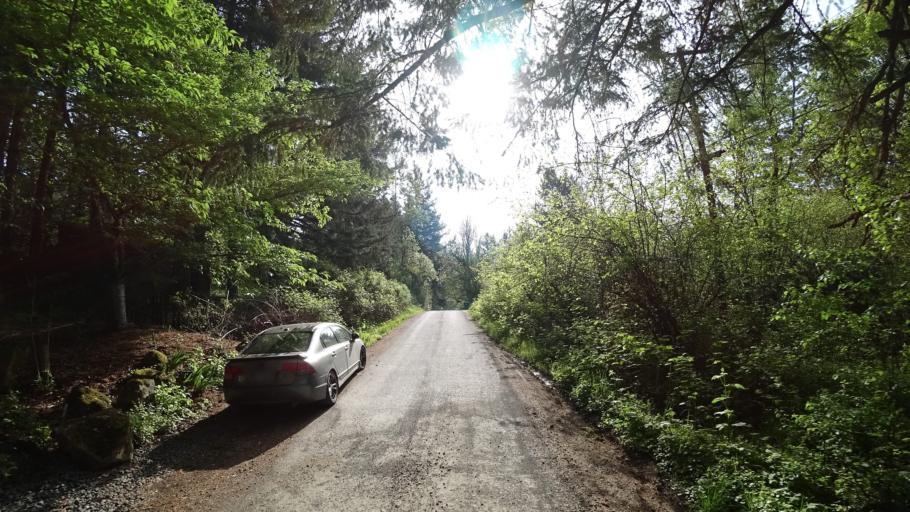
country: US
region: Oregon
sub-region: Washington County
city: King City
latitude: 45.4346
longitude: -122.8500
